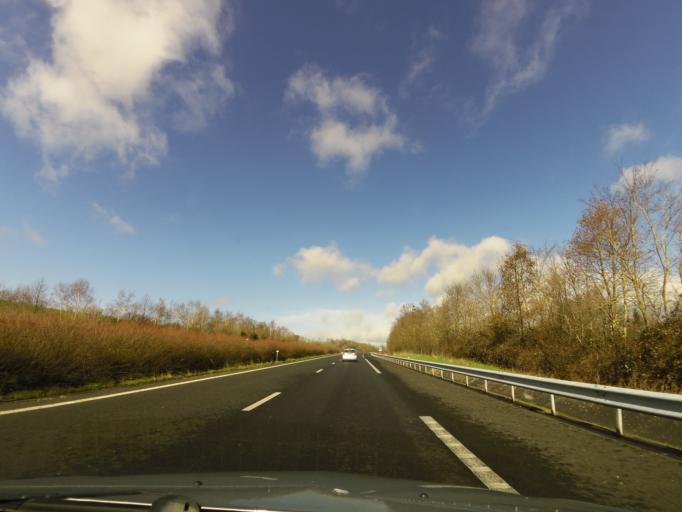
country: FR
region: Lower Normandy
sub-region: Departement de la Manche
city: Torigni-sur-Vire
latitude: 49.0221
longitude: -0.9798
